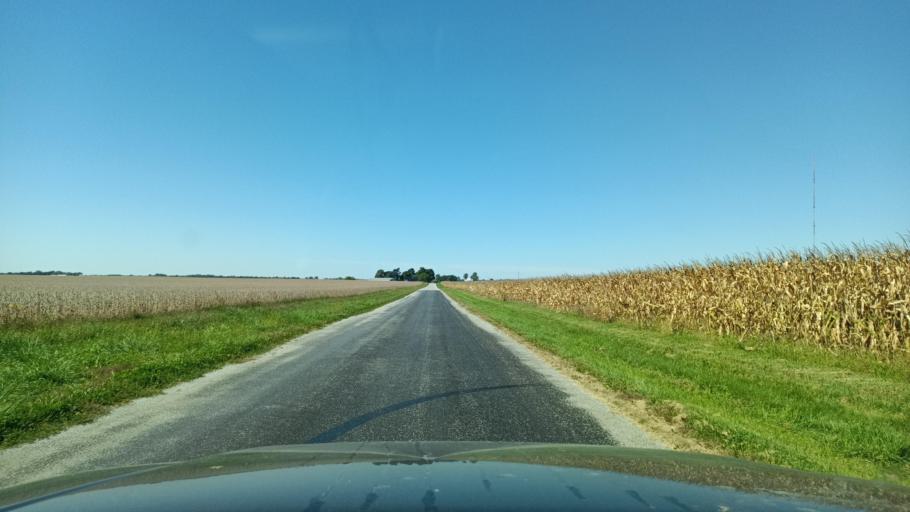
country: US
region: Illinois
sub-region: Champaign County
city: Mahomet
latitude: 40.0986
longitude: -88.4329
